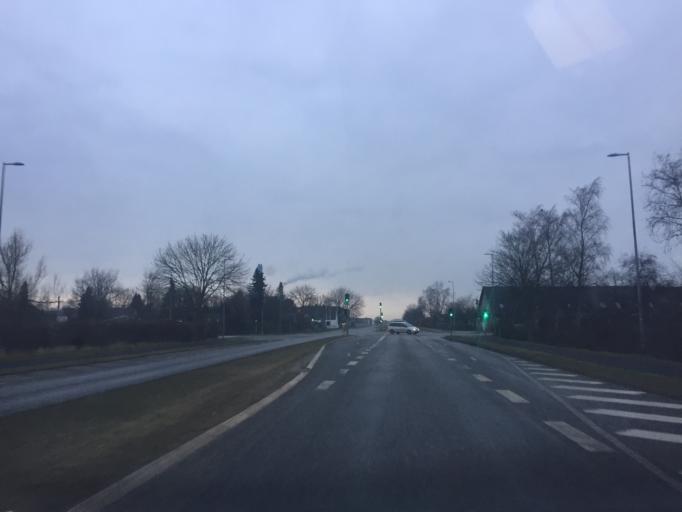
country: DK
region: Zealand
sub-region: Solrod Kommune
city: Solrod Strand
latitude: 55.5345
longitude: 12.2073
